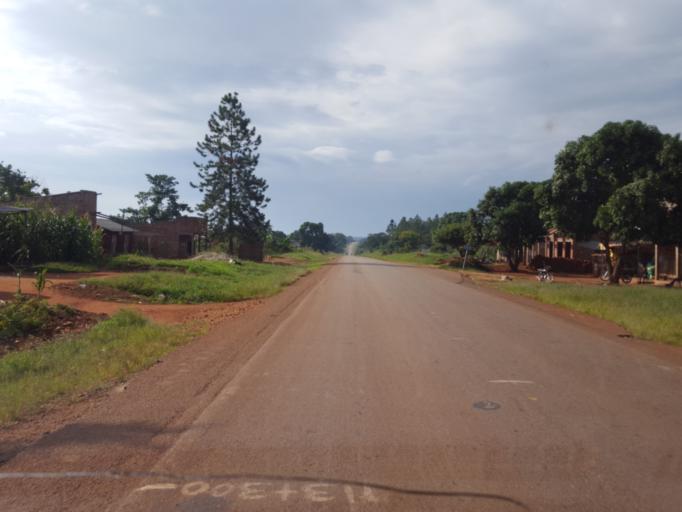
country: UG
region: Western Region
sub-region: Hoima District
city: Hoima
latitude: 1.2373
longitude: 31.5350
